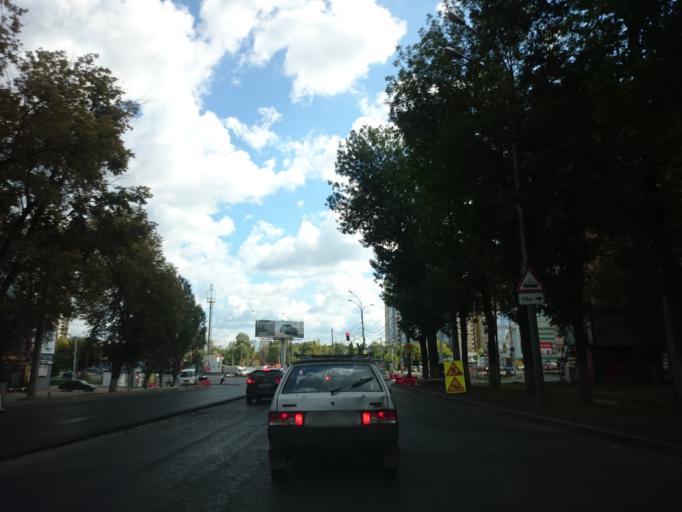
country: RU
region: Samara
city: Samara
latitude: 53.2197
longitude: 50.1621
